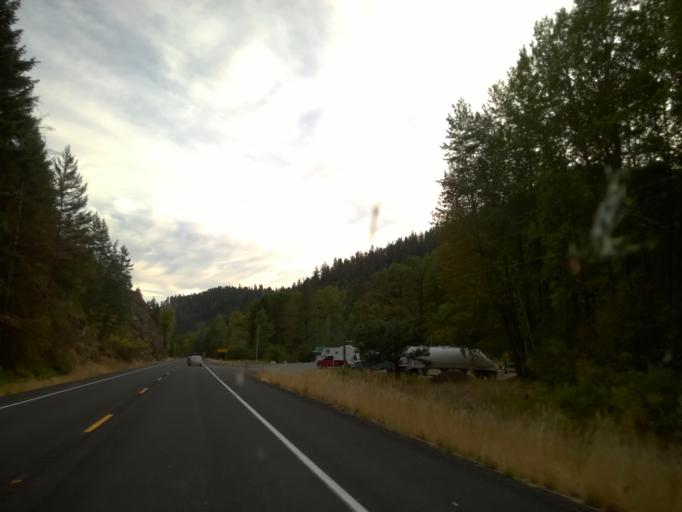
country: US
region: Washington
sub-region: Kittitas County
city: Cle Elum
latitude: 47.2227
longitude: -120.6973
